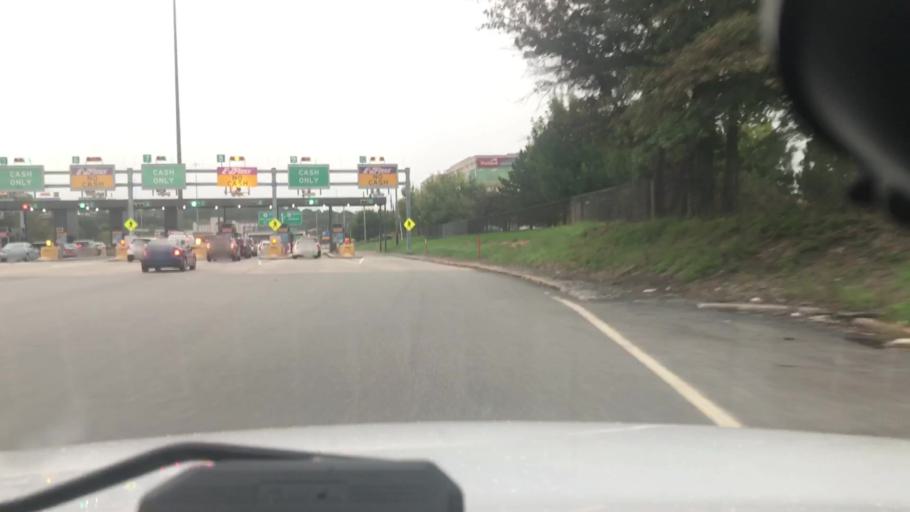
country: US
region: Pennsylvania
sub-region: Montgomery County
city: Fort Washington
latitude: 40.1347
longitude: -75.1961
